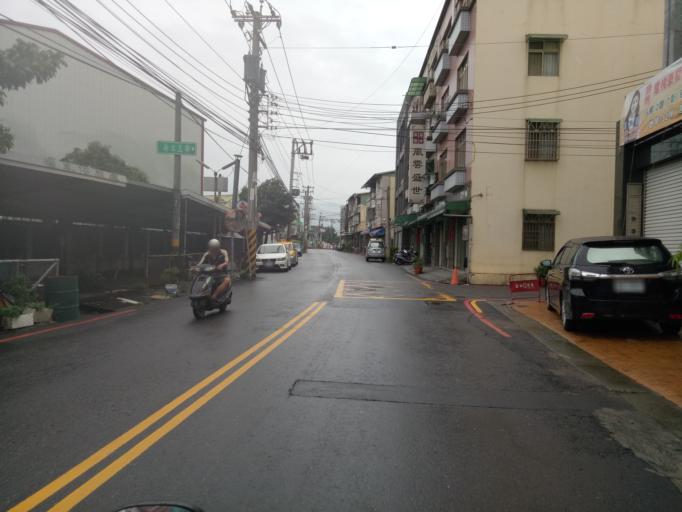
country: TW
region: Taiwan
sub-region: Taichung City
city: Taichung
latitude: 24.1113
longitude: 120.7084
